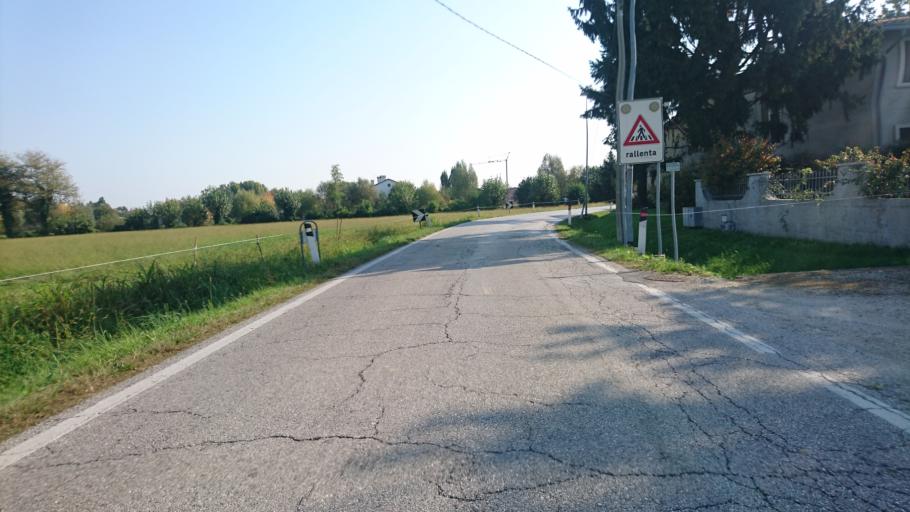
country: IT
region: Veneto
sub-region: Provincia di Padova
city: Gazzo
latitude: 45.5865
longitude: 11.7037
